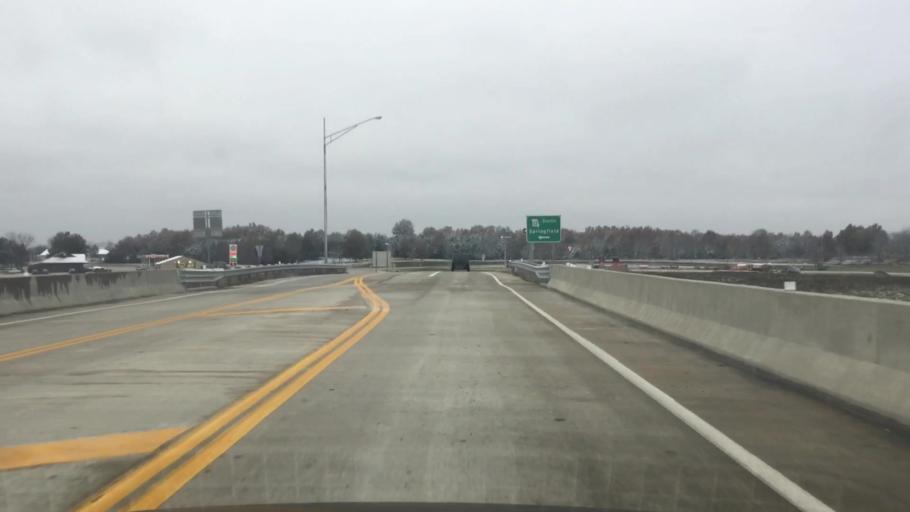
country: US
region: Missouri
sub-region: Saint Clair County
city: Osceola
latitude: 38.0406
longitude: -93.6816
